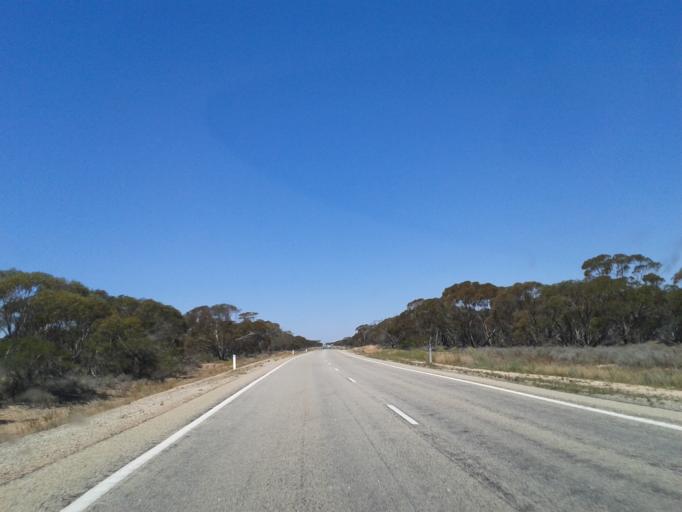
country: AU
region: New South Wales
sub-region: Wentworth
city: Gol Gol
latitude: -34.4726
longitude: 142.5518
